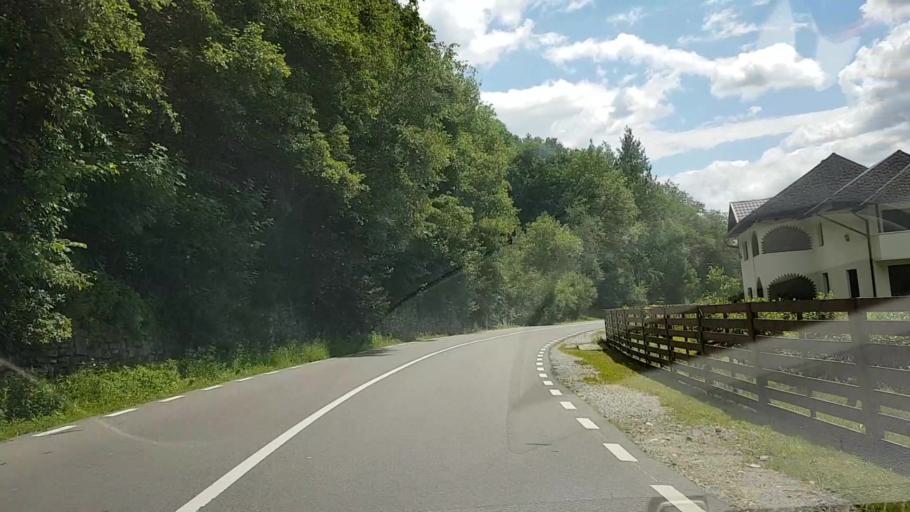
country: RO
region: Suceava
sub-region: Comuna Brosteni
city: Brosteni
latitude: 47.2601
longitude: 25.6894
